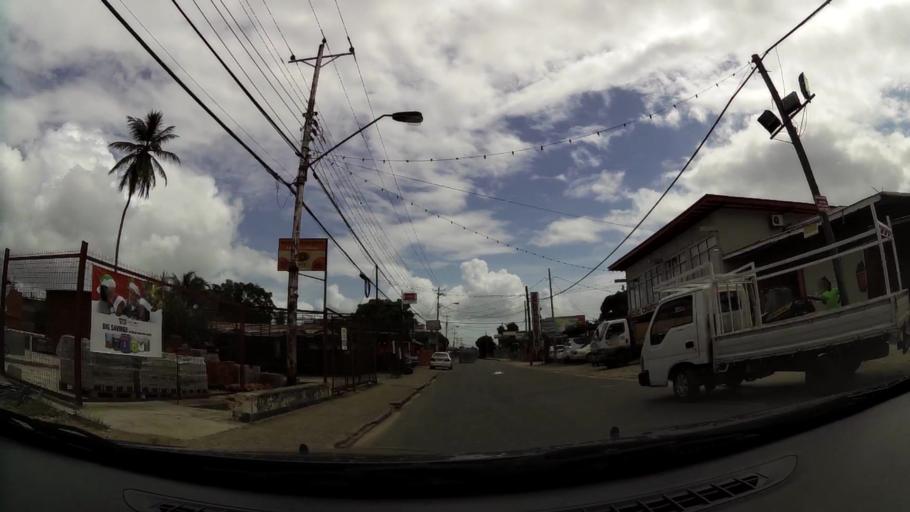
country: TT
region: Tunapuna/Piarco
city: Arouca
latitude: 10.6336
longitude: -61.3270
